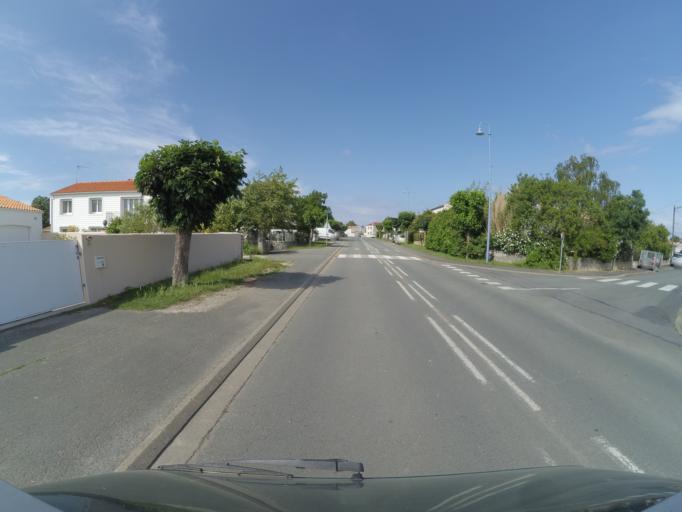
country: FR
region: Poitou-Charentes
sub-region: Departement de la Charente-Maritime
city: Andilly
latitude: 46.2393
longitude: -1.0686
